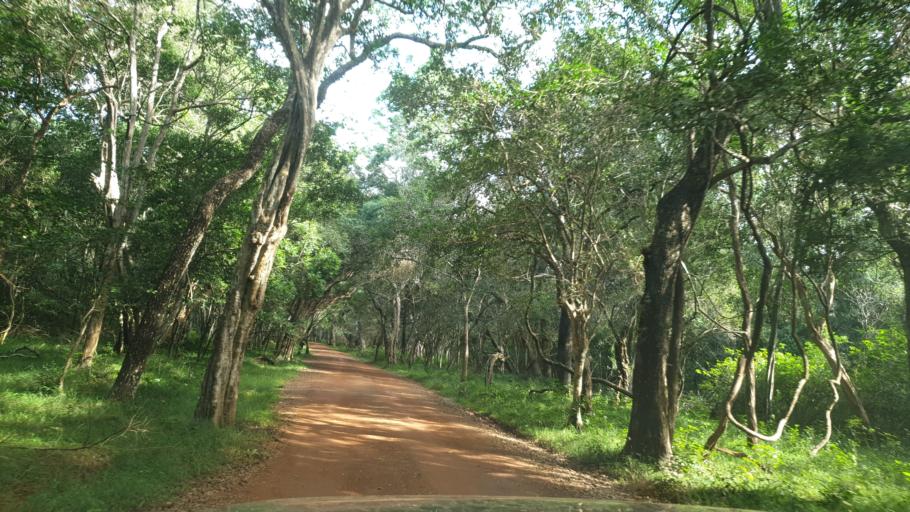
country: LK
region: North Central
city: Anuradhapura
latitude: 8.3819
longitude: 80.0630
